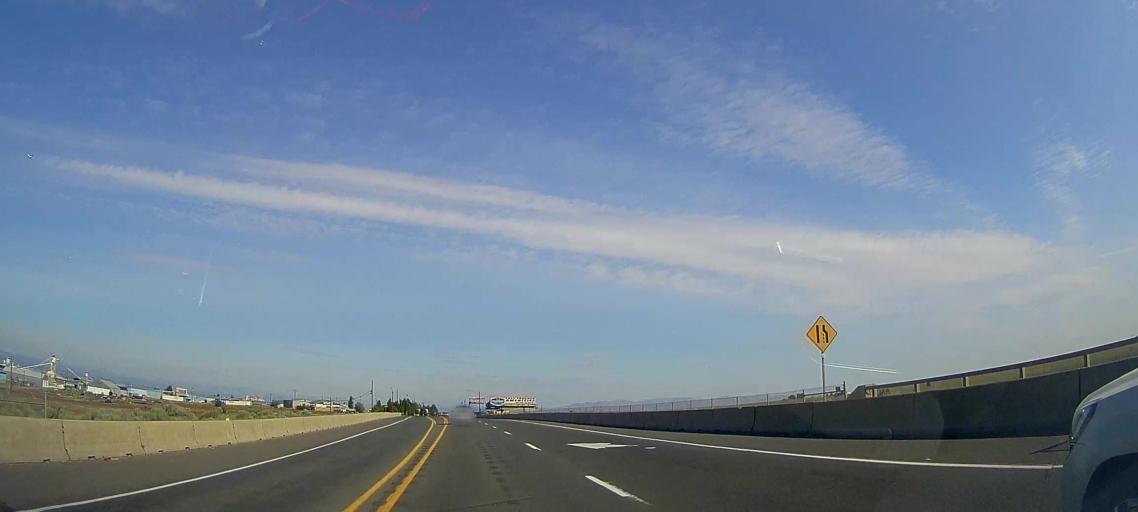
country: US
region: Oregon
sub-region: Jefferson County
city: Madras
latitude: 44.6560
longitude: -121.1293
